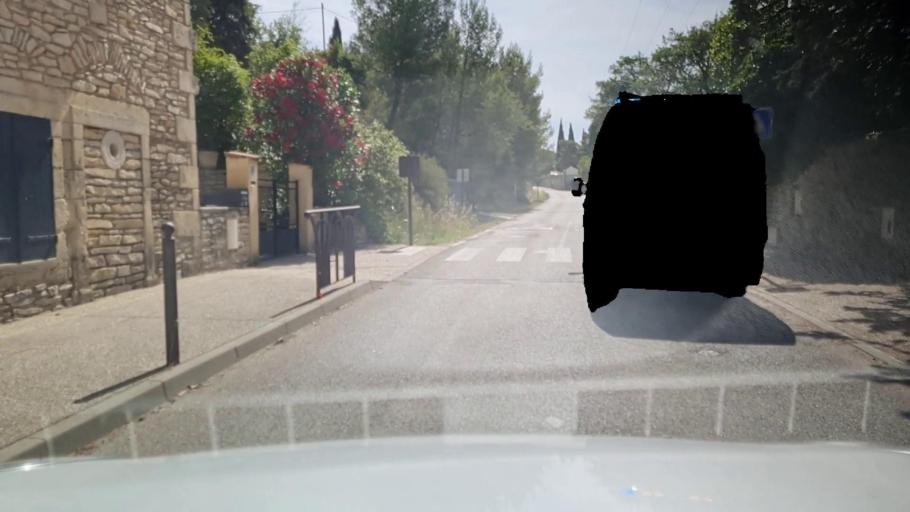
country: FR
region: Languedoc-Roussillon
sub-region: Departement du Gard
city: Nages-et-Solorgues
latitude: 43.7895
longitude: 4.2316
